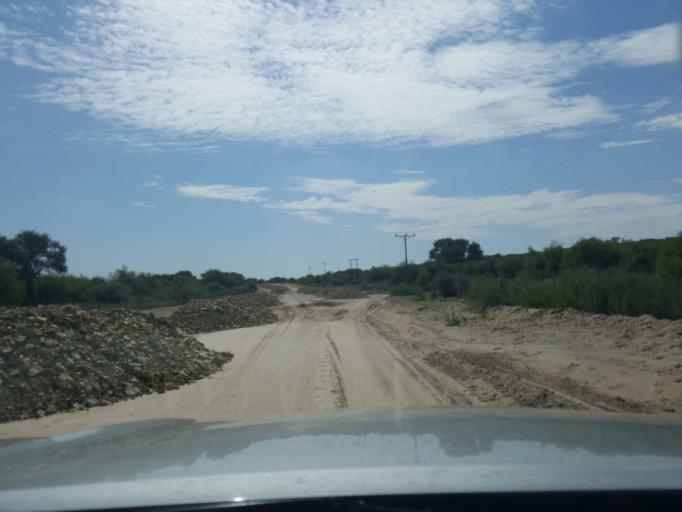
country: BW
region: Kweneng
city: Letlhakeng
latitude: -24.0453
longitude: 25.0166
